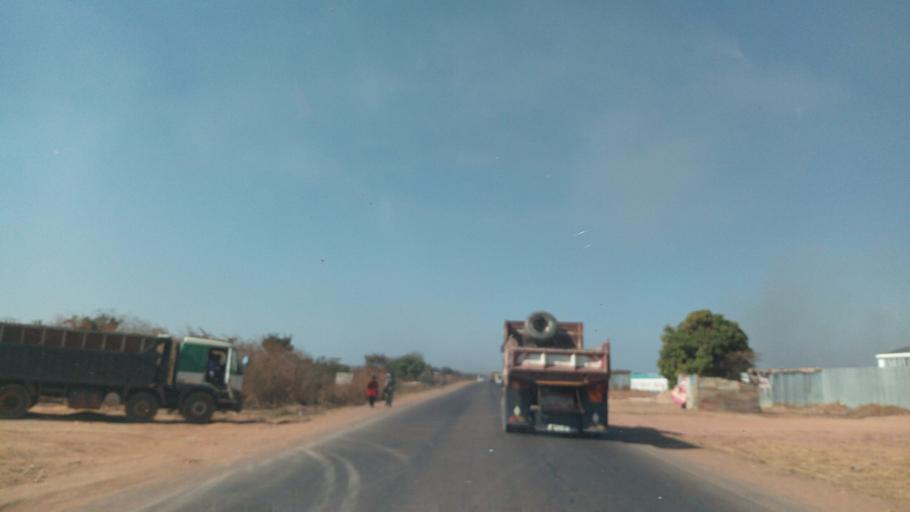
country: CD
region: Katanga
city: Lubumbashi
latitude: -11.5767
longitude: 27.5323
